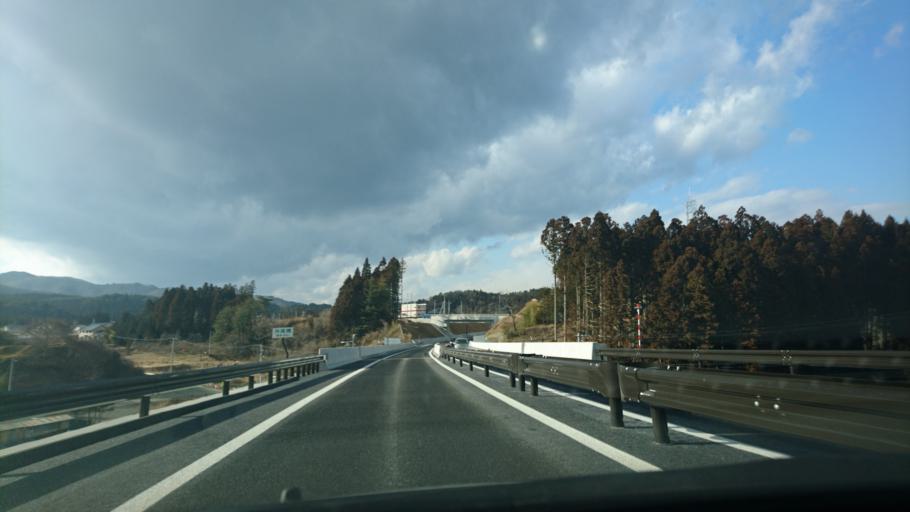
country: JP
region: Miyagi
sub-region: Oshika Gun
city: Onagawa Cho
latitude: 38.7608
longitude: 141.5006
